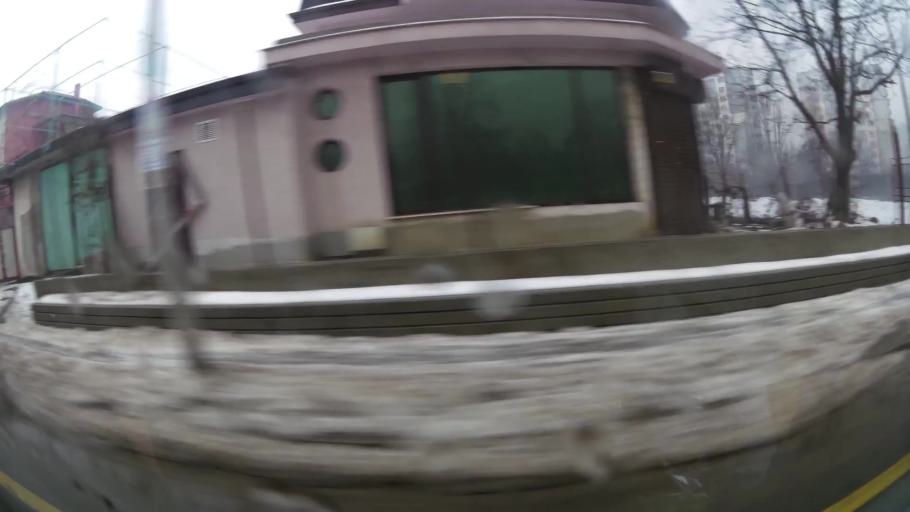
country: BG
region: Sofia-Capital
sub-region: Stolichna Obshtina
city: Sofia
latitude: 42.6743
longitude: 23.2525
